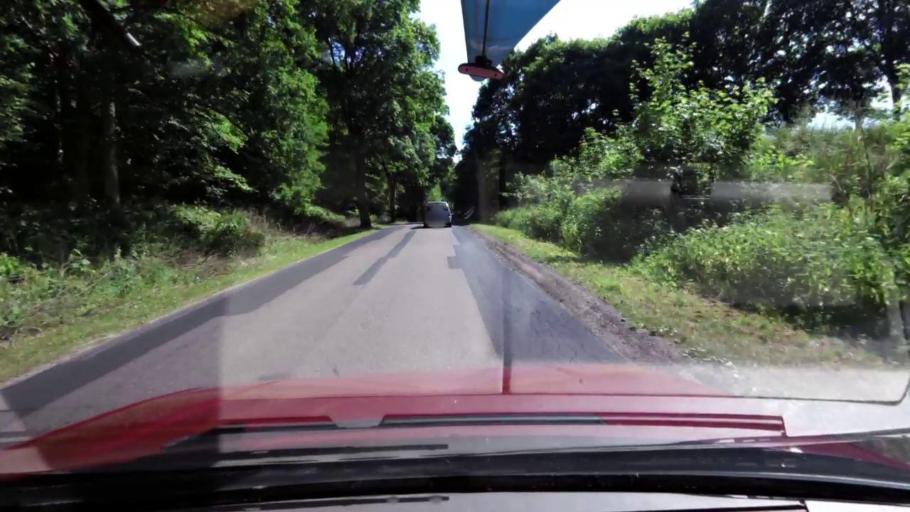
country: PL
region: Pomeranian Voivodeship
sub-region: Powiat slupski
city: Kepice
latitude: 54.2613
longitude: 16.9443
